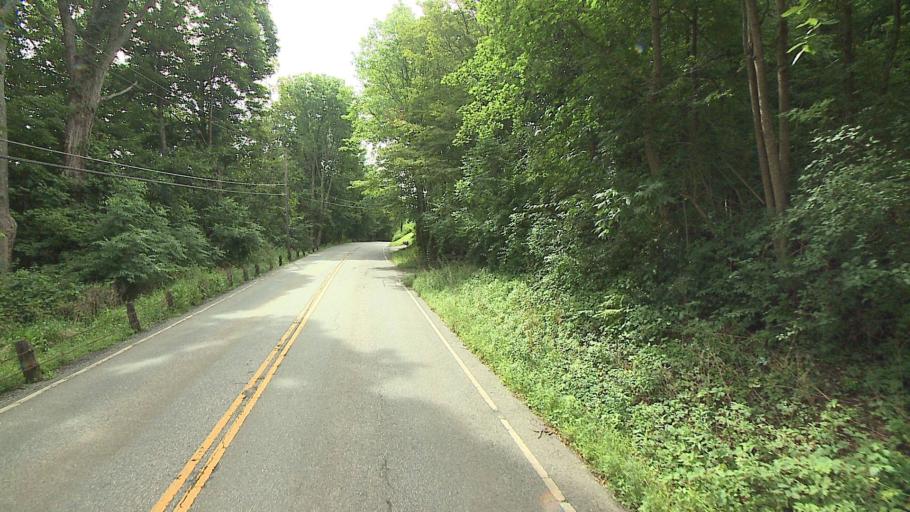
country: US
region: Connecticut
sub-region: Litchfield County
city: Kent
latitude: 41.7402
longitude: -73.4972
